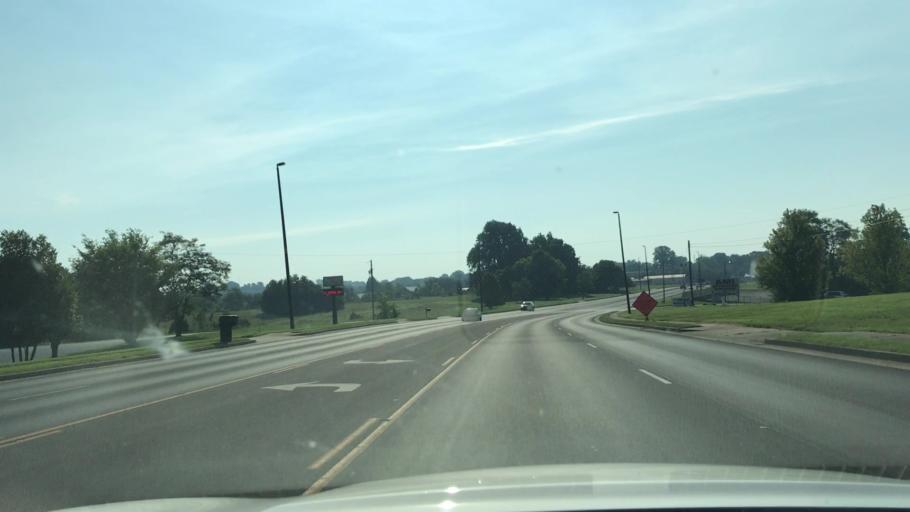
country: US
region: Kentucky
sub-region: Barren County
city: Glasgow
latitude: 37.0100
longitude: -85.9428
